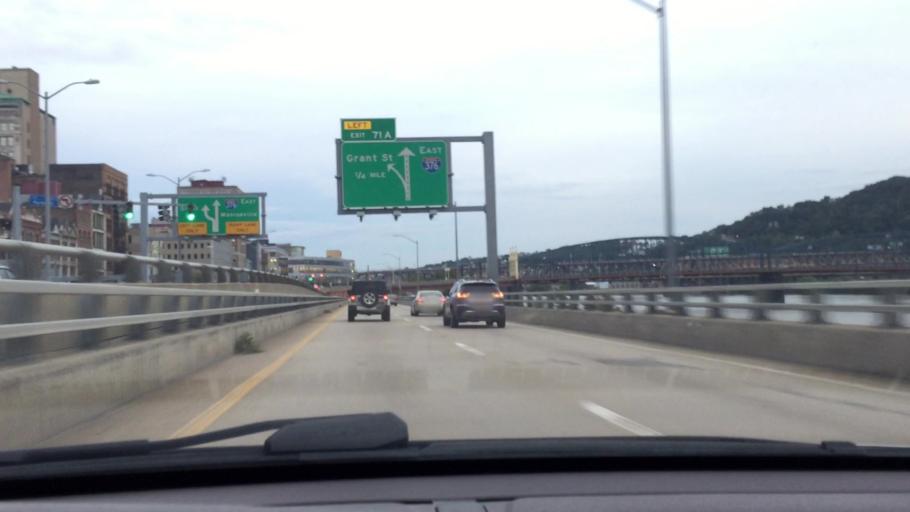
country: US
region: Pennsylvania
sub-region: Allegheny County
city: Pittsburgh
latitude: 40.4379
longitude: -80.0051
